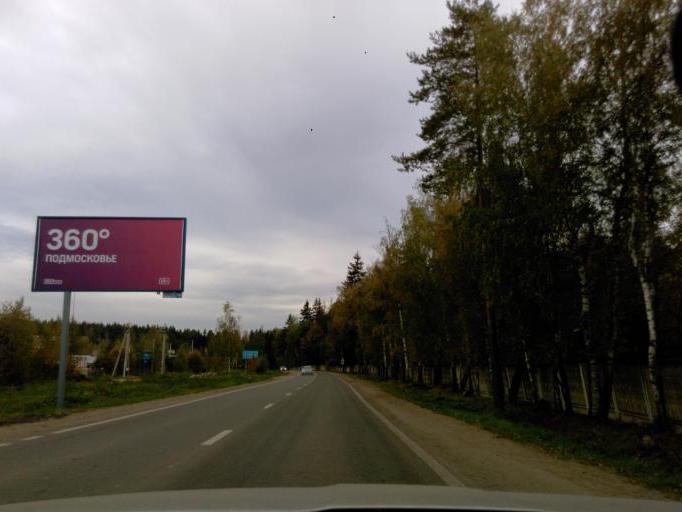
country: RU
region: Moskovskaya
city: Andreyevka
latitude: 55.9789
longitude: 37.1191
